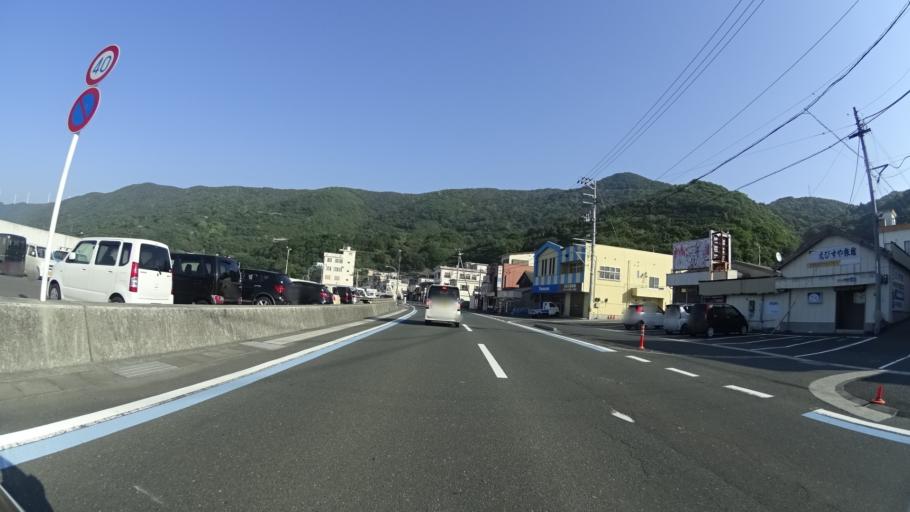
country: JP
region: Ehime
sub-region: Nishiuwa-gun
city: Ikata-cho
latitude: 33.3894
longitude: 132.1204
